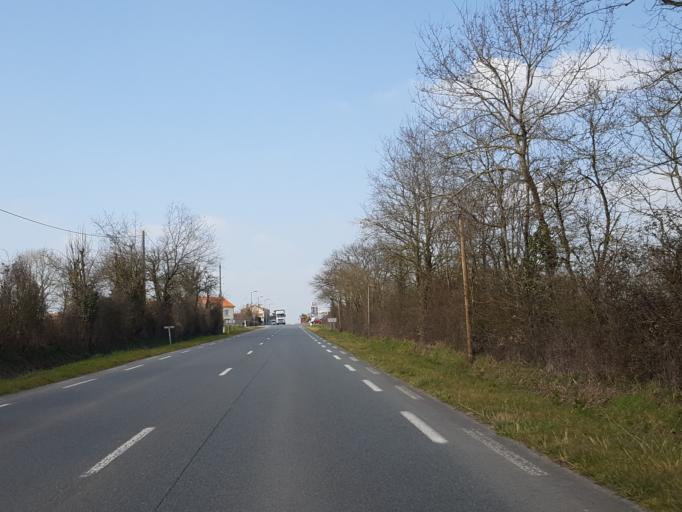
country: FR
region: Pays de la Loire
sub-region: Departement de la Vendee
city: La Chaize-le-Vicomte
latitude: 46.6680
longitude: -1.2832
